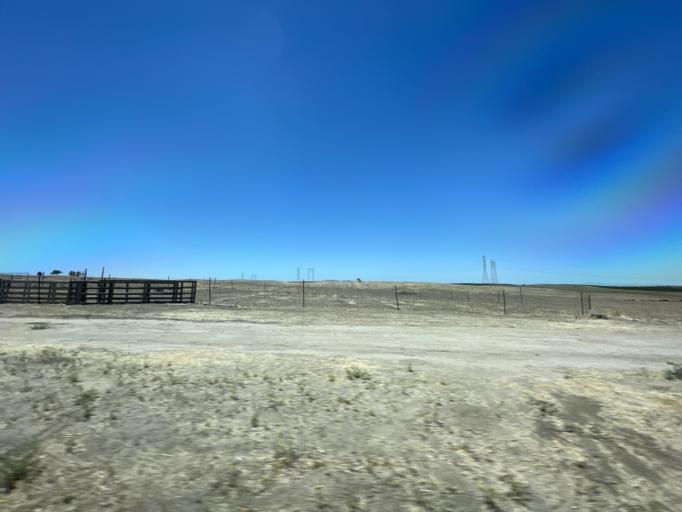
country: US
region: California
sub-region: San Luis Obispo County
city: Paso Robles
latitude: 35.6502
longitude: -120.5789
